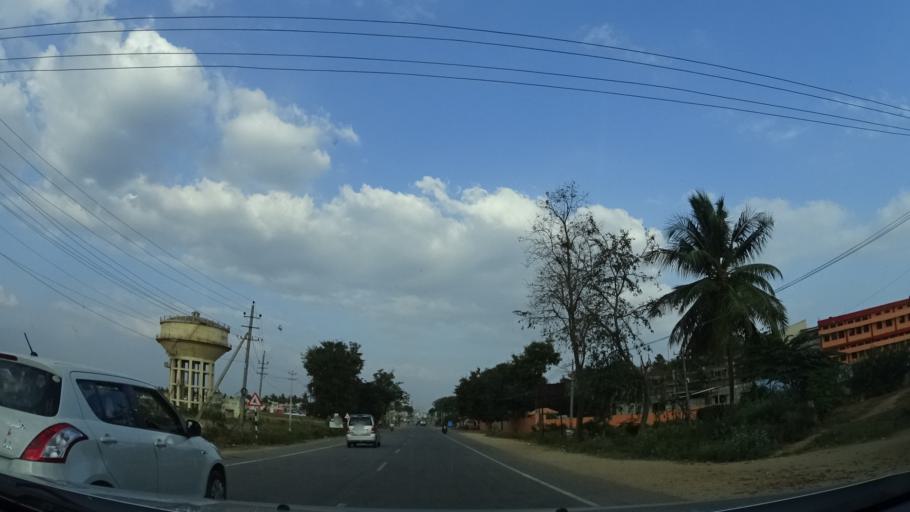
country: IN
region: Karnataka
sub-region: Mandya
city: Malavalli
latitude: 12.3801
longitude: 77.0445
